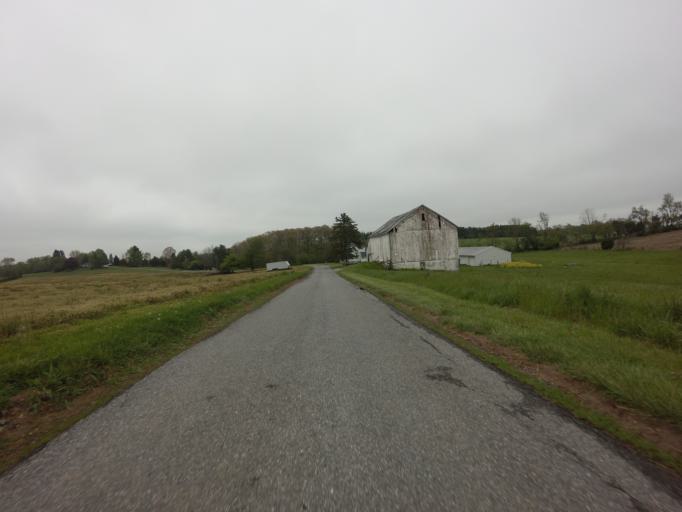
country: US
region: Maryland
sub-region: Carroll County
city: Hampstead
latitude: 39.5787
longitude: -76.7703
